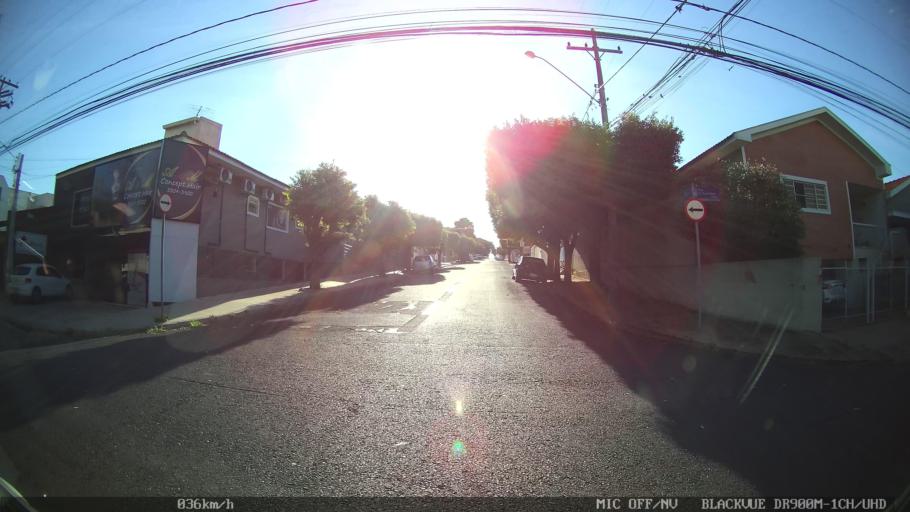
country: BR
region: Sao Paulo
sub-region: Sao Jose Do Rio Preto
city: Sao Jose do Rio Preto
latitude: -20.8212
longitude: -49.4008
